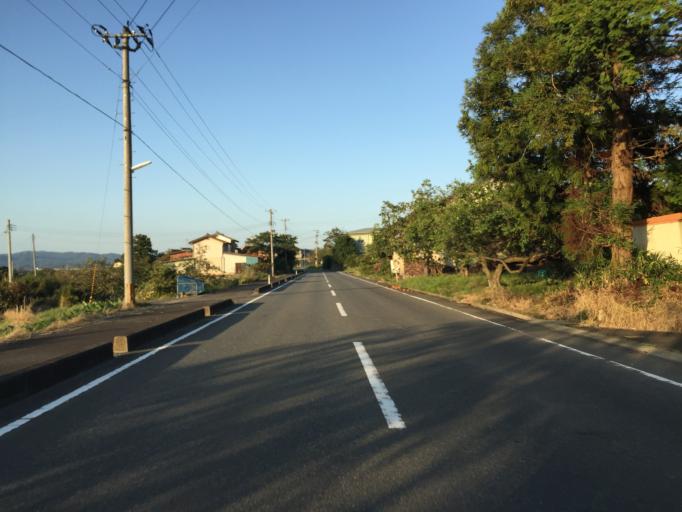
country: JP
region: Fukushima
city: Hobaramachi
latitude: 37.8156
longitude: 140.5842
